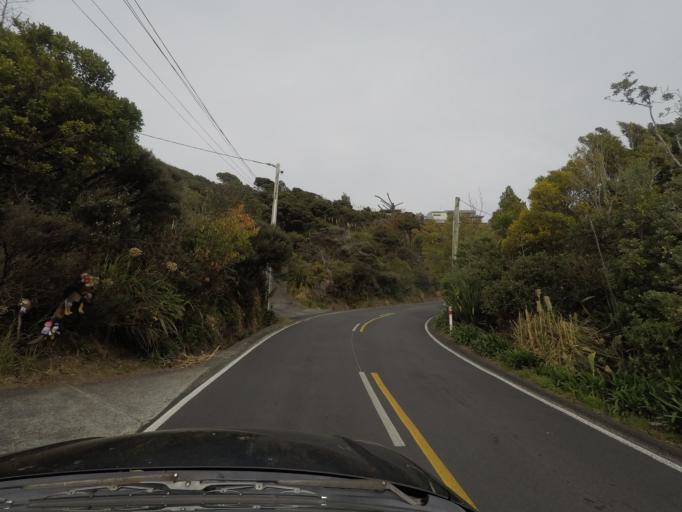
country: NZ
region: Auckland
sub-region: Auckland
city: Muriwai Beach
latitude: -36.9616
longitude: 174.4751
